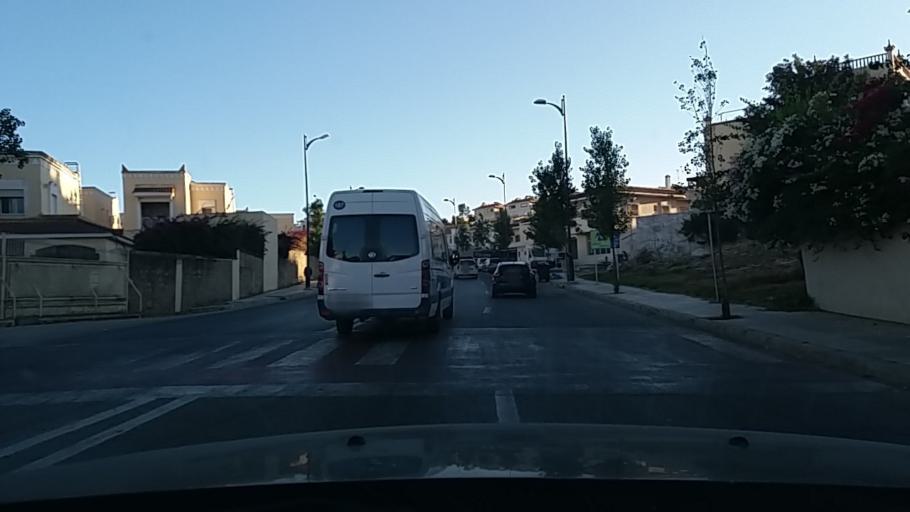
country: MA
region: Tanger-Tetouan
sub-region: Tanger-Assilah
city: Boukhalef
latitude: 35.7723
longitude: -5.8582
